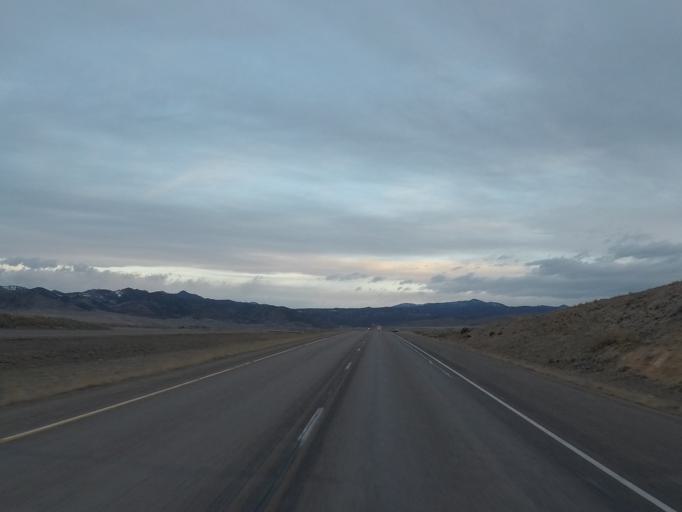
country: US
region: Montana
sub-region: Jefferson County
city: Whitehall
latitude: 45.8947
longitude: -112.1841
